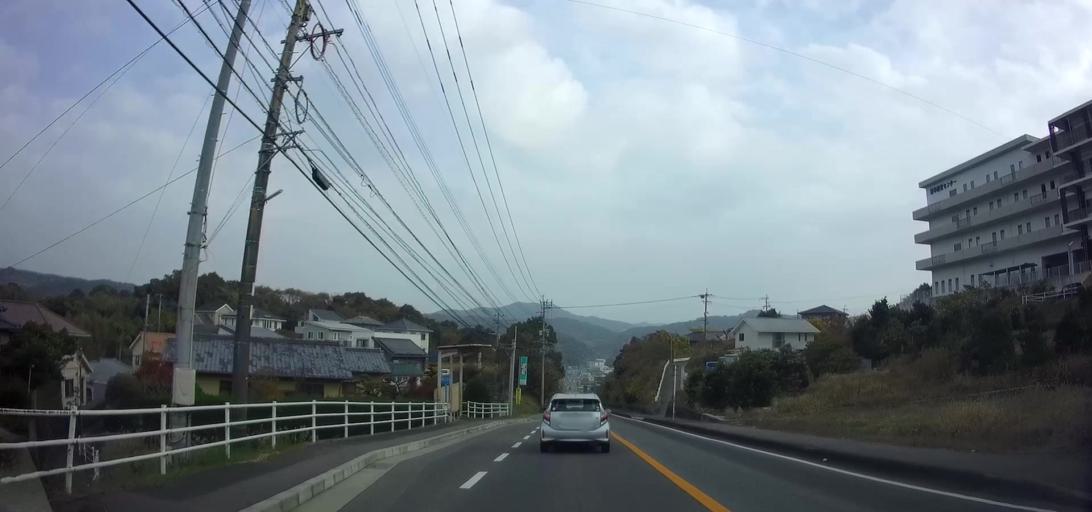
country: JP
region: Nagasaki
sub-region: Isahaya-shi
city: Isahaya
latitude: 32.7937
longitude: 130.0767
